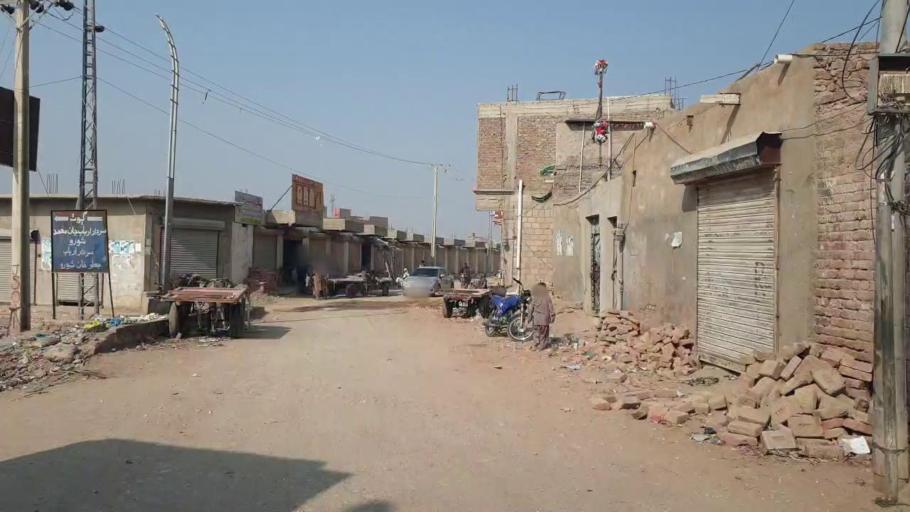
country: PK
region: Sindh
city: Kotri
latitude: 25.3622
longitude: 68.3137
